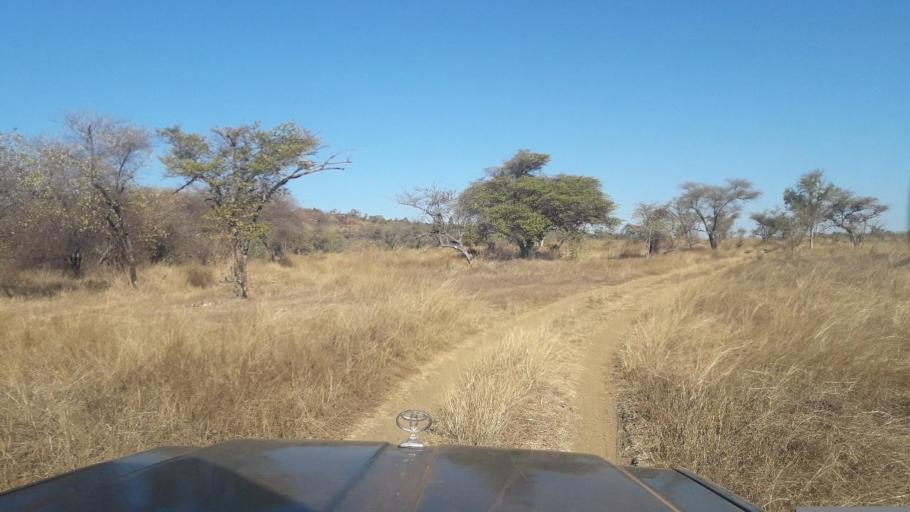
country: MG
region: Boeny
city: Sitampiky
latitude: -16.3890
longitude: 45.5915
